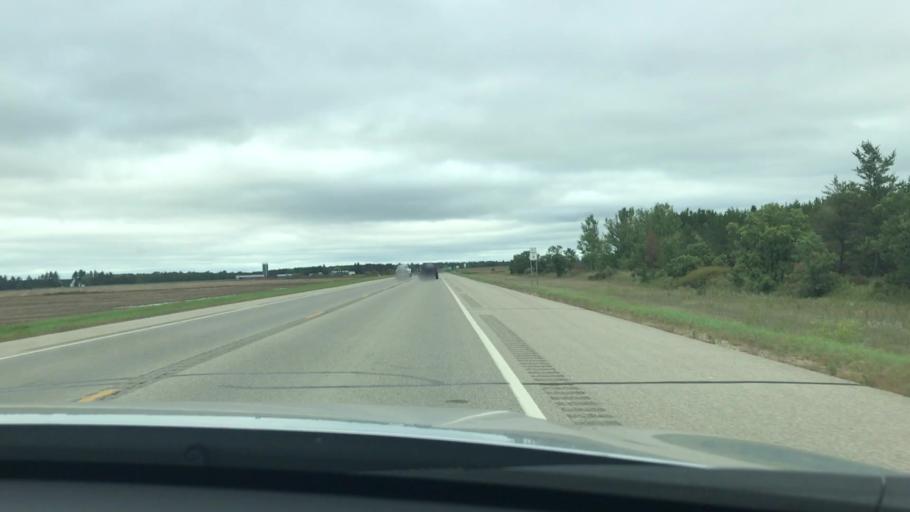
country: US
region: Minnesota
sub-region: Hubbard County
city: Park Rapids
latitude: 46.8536
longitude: -95.0769
